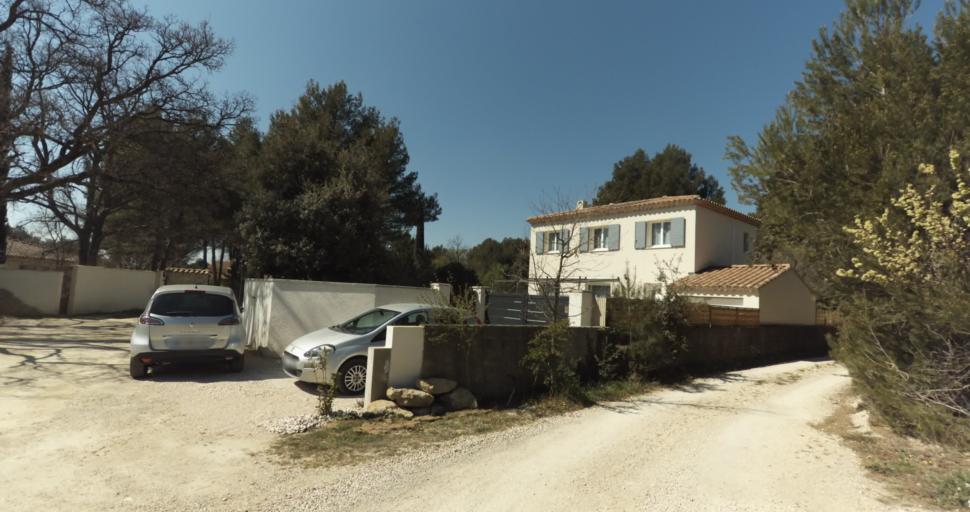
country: FR
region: Provence-Alpes-Cote d'Azur
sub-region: Departement des Bouches-du-Rhone
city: Pelissanne
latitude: 43.6313
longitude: 5.1698
